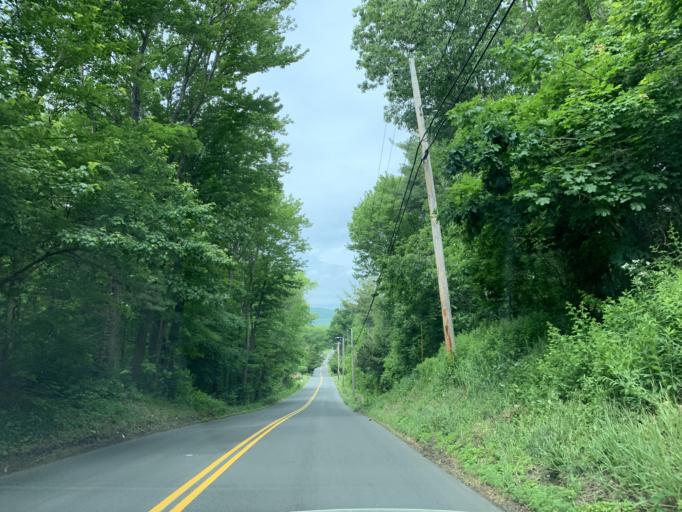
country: US
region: Massachusetts
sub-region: Hampshire County
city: Southampton
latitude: 42.1845
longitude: -72.7367
